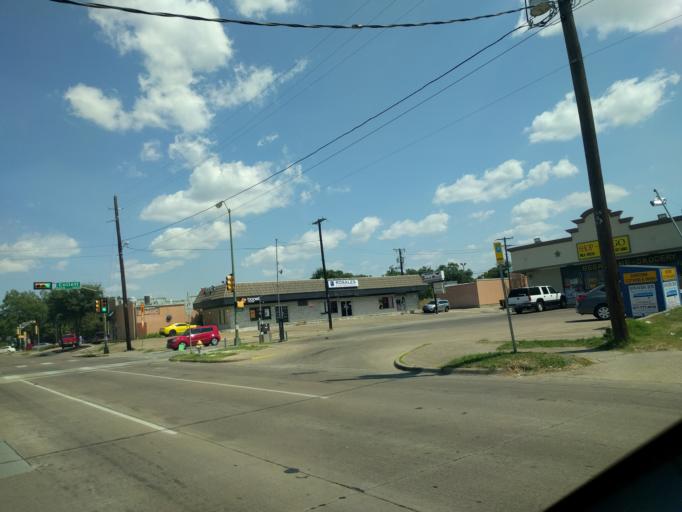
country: US
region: Texas
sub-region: Dallas County
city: Dallas
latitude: 32.7963
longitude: -96.7622
